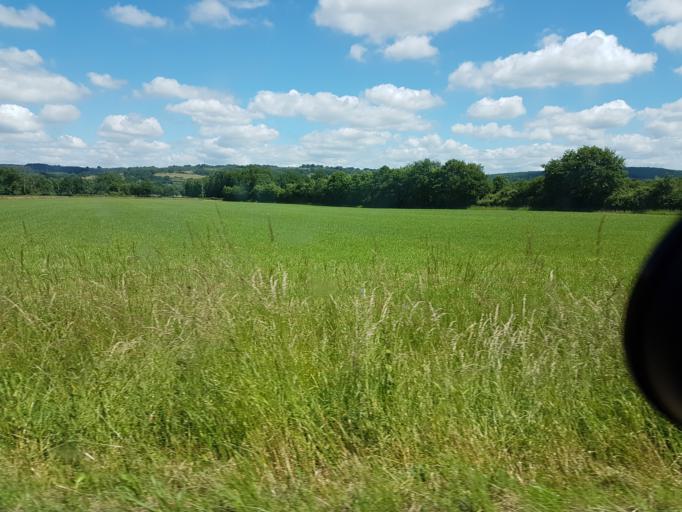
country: FR
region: Bourgogne
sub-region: Departement de Saone-et-Loire
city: Epinac
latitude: 47.0068
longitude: 4.4611
